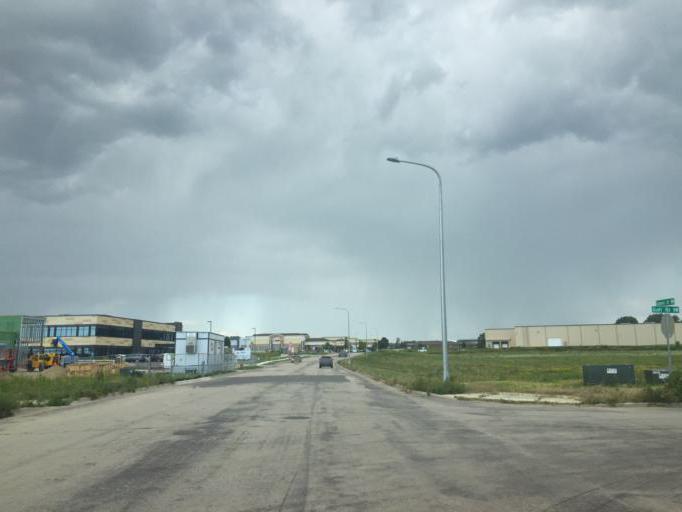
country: US
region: Minnesota
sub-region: Olmsted County
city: Rochester
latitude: 44.0488
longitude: -92.5195
